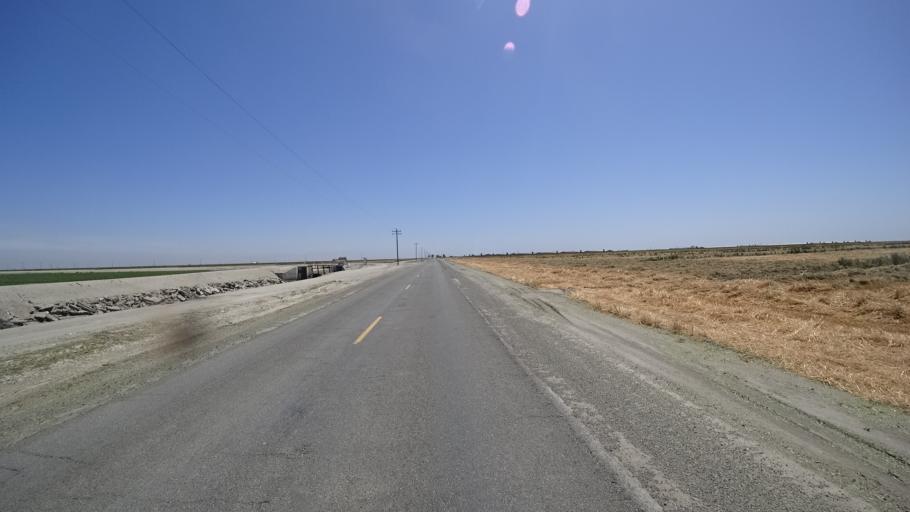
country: US
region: California
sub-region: Kings County
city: Corcoran
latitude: 36.1379
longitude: -119.6742
